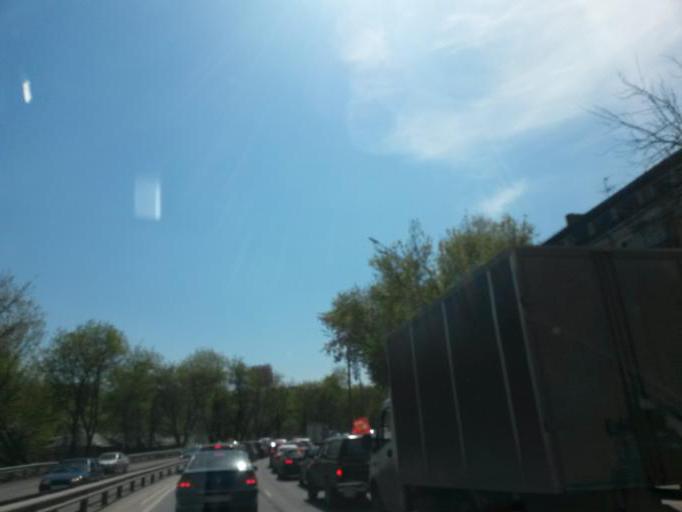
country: RU
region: Moskovskaya
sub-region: Podol'skiy Rayon
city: Podol'sk
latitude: 55.4399
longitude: 37.5563
